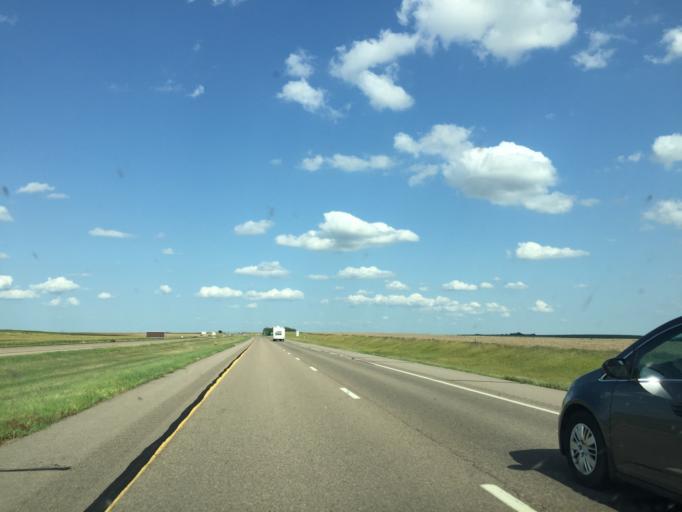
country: US
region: Kansas
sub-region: Trego County
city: WaKeeney
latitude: 39.0235
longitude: -100.1017
